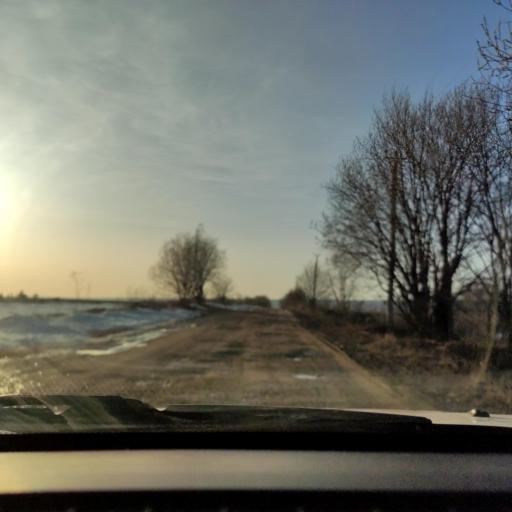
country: RU
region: Perm
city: Novyye Lyady
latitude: 58.1477
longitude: 56.5023
